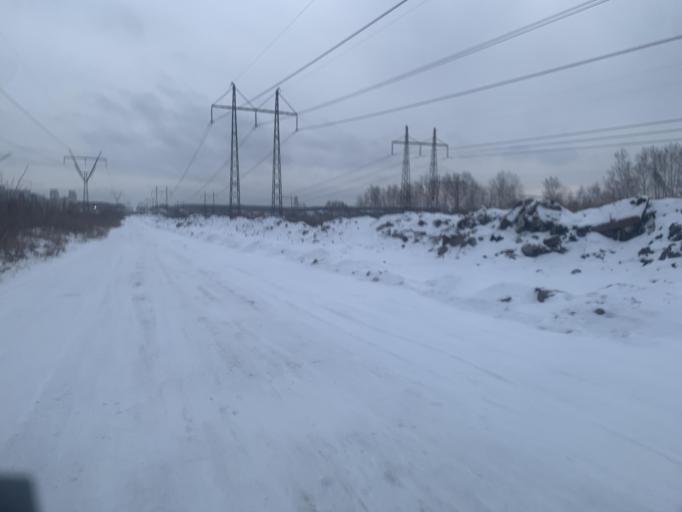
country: RU
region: Chelyabinsk
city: Roshchino
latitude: 55.1899
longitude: 61.2587
